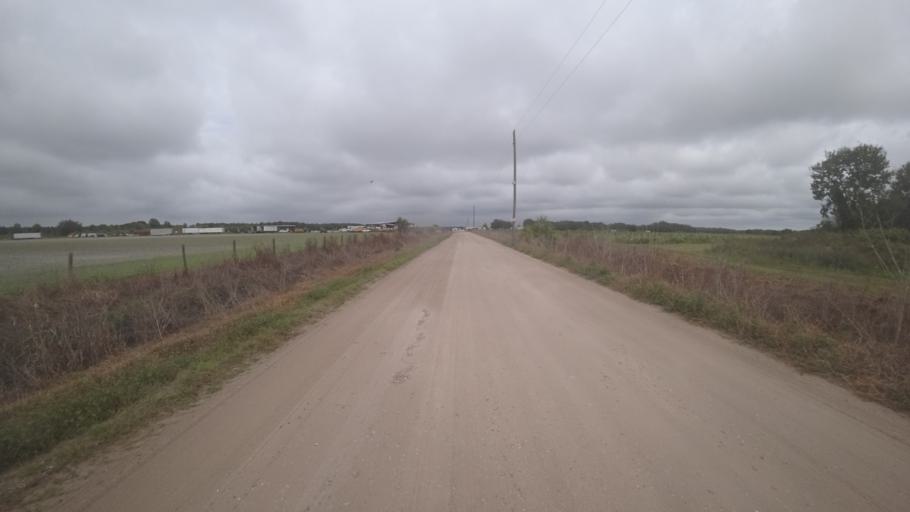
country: US
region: Florida
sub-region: Sarasota County
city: Warm Mineral Springs
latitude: 27.2776
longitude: -82.1699
